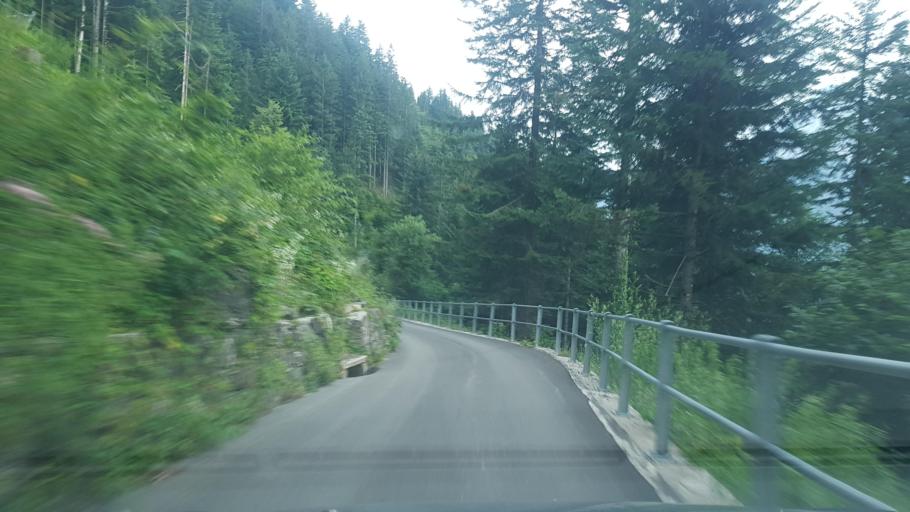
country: IT
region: Friuli Venezia Giulia
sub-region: Provincia di Udine
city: Paularo
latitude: 46.5500
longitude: 13.1230
